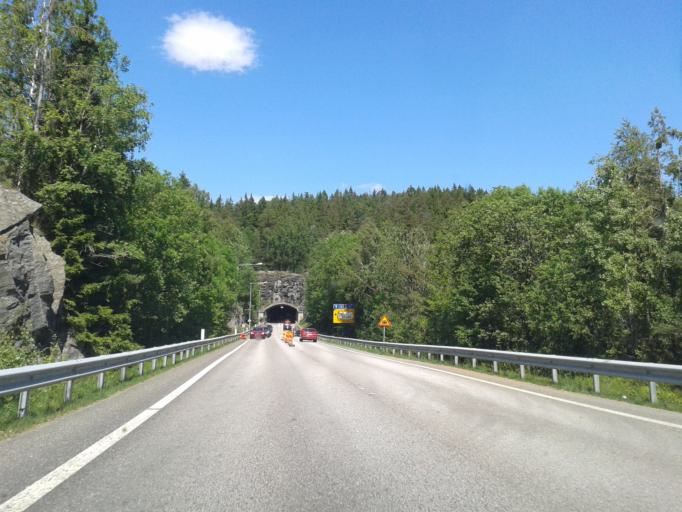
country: SE
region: Vaestra Goetaland
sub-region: Orust
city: Henan
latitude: 58.2959
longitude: 11.7021
